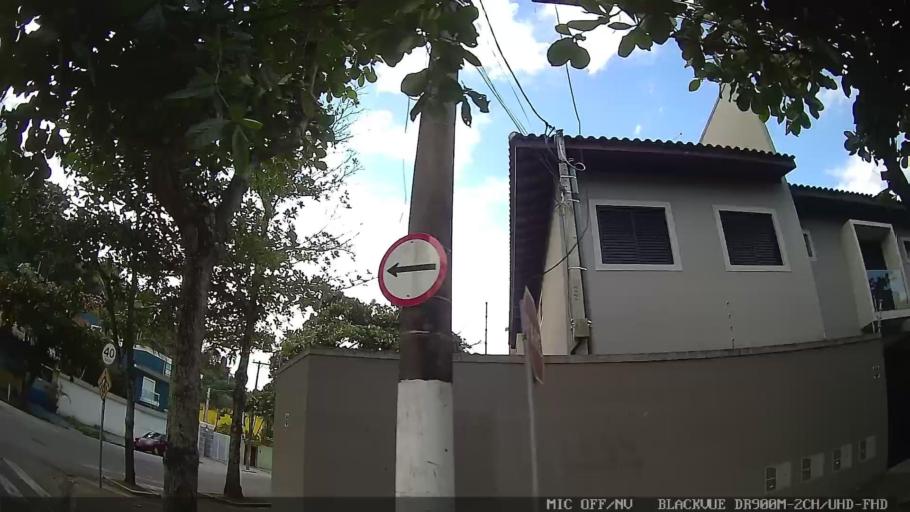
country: BR
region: Sao Paulo
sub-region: Guaruja
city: Guaruja
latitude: -23.9873
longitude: -46.2394
